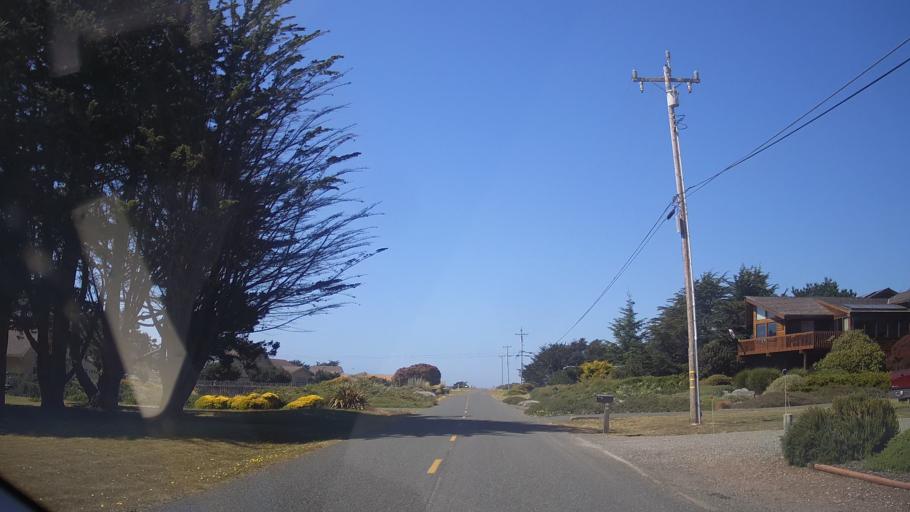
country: US
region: California
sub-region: Mendocino County
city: Fort Bragg
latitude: 39.4219
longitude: -123.8137
